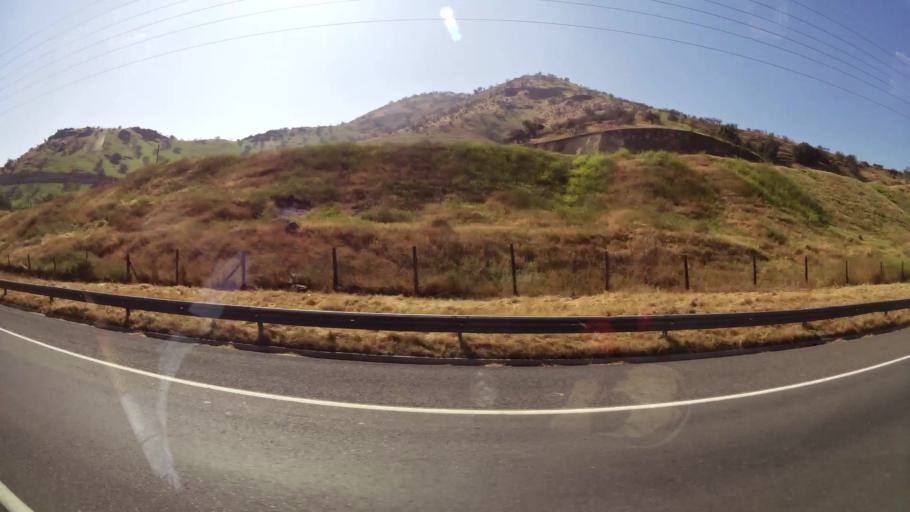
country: CL
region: Santiago Metropolitan
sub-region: Provincia de Chacabuco
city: Chicureo Abajo
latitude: -33.3220
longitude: -70.7059
